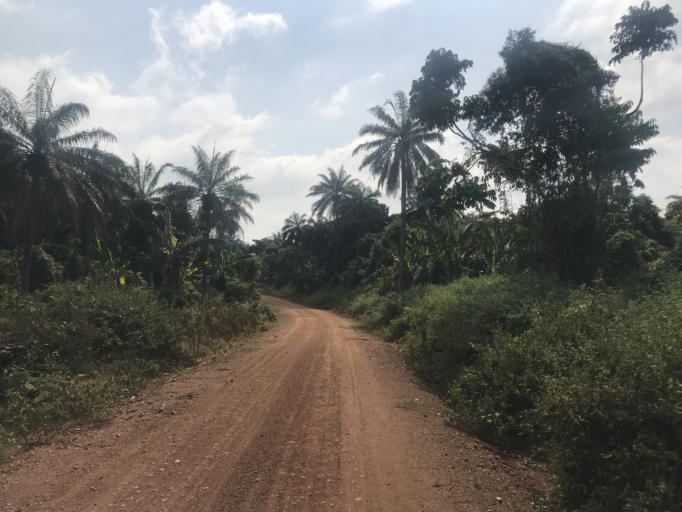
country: NG
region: Osun
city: Ibokun
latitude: 7.8167
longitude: 4.6451
